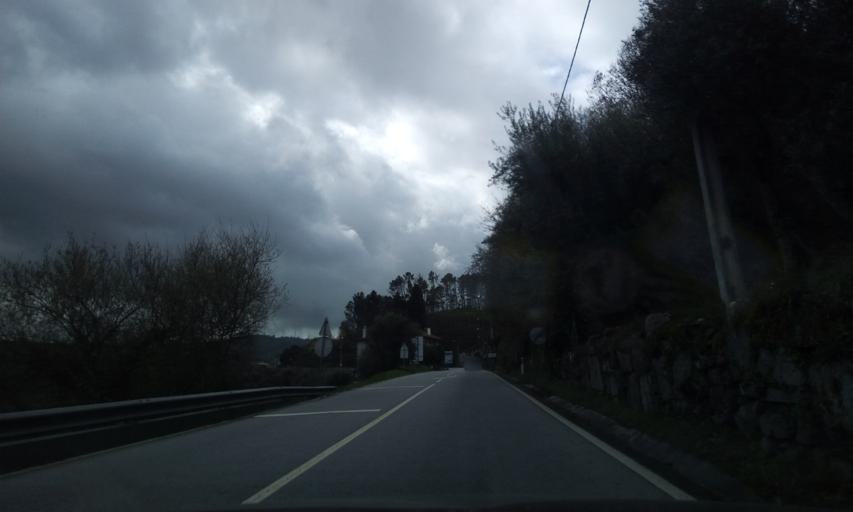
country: PT
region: Viseu
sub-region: Mangualde
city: Mangualde
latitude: 40.6381
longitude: -7.7399
